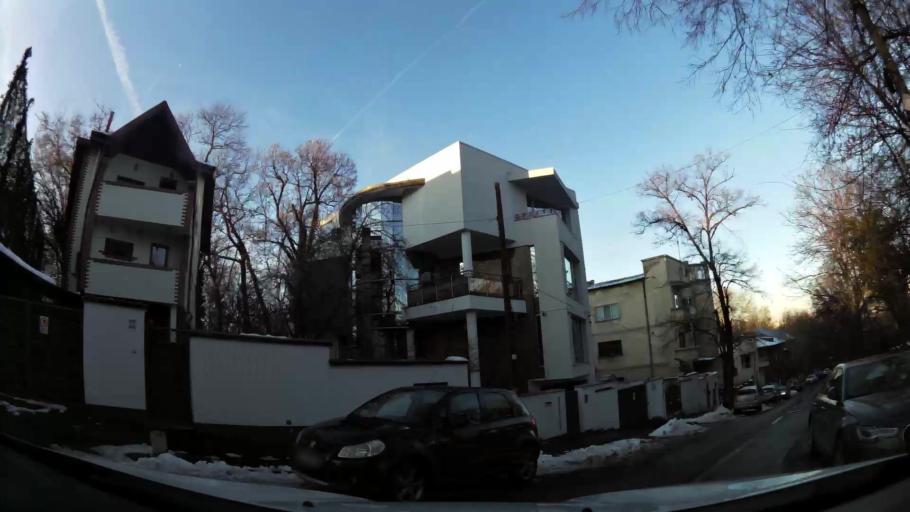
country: RO
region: Bucuresti
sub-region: Municipiul Bucuresti
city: Bucuresti
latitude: 44.4315
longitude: 26.0632
